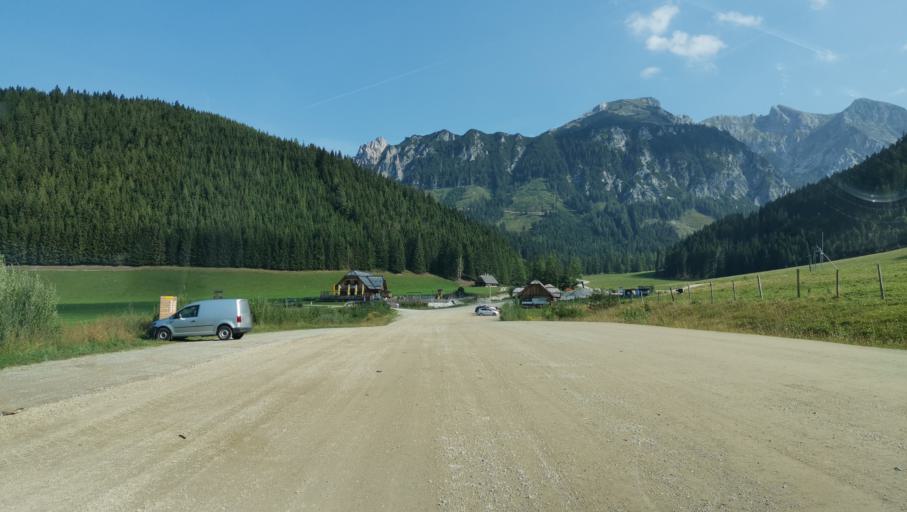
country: AT
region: Styria
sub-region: Politischer Bezirk Liezen
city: Trieben
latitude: 47.5276
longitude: 14.4842
